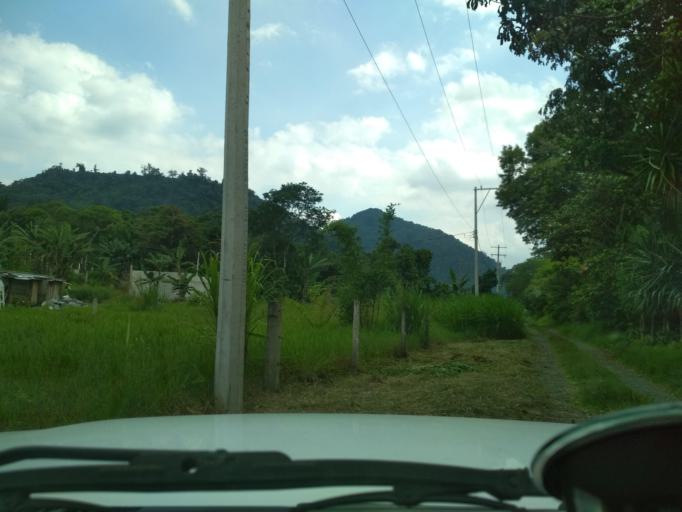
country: MX
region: Veracruz
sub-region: Ixtaczoquitlan
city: Buenavista
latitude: 18.8999
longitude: -97.0278
